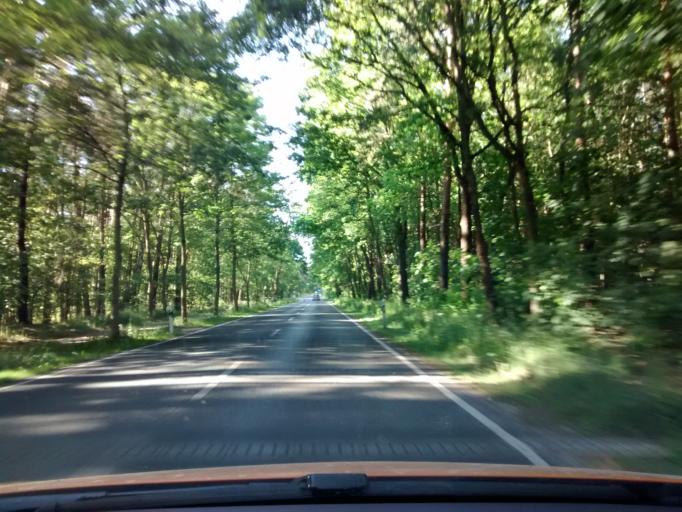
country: DE
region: Brandenburg
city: Bad Saarow
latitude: 52.2982
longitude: 14.0631
